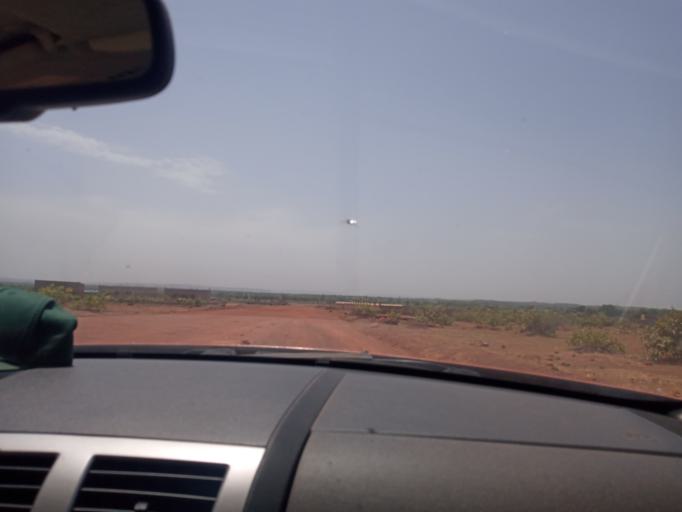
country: ML
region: Bamako
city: Bamako
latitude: 12.5166
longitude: -7.7909
